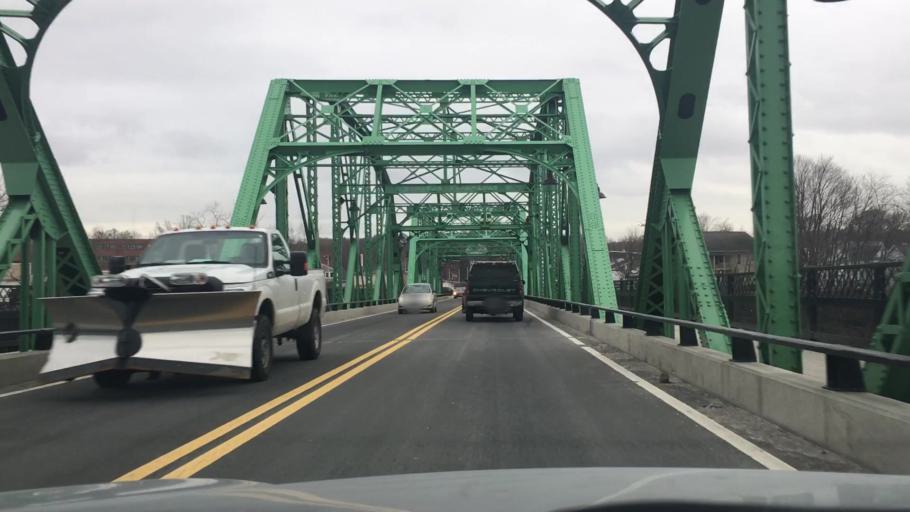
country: US
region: Massachusetts
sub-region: Hampden County
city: North Chicopee
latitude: 42.1945
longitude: -72.6010
